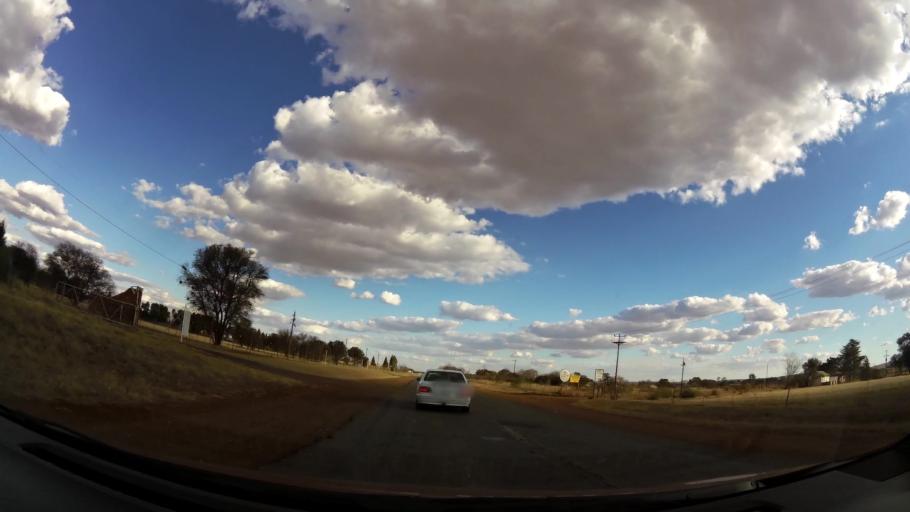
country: ZA
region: North-West
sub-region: Dr Kenneth Kaunda District Municipality
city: Potchefstroom
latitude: -26.6271
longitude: 27.1091
